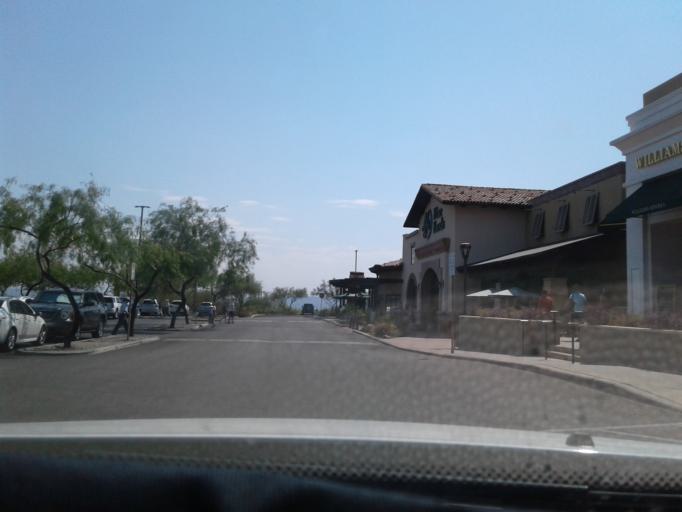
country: US
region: Arizona
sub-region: Pima County
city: Catalina Foothills
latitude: 32.3245
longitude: -110.9310
